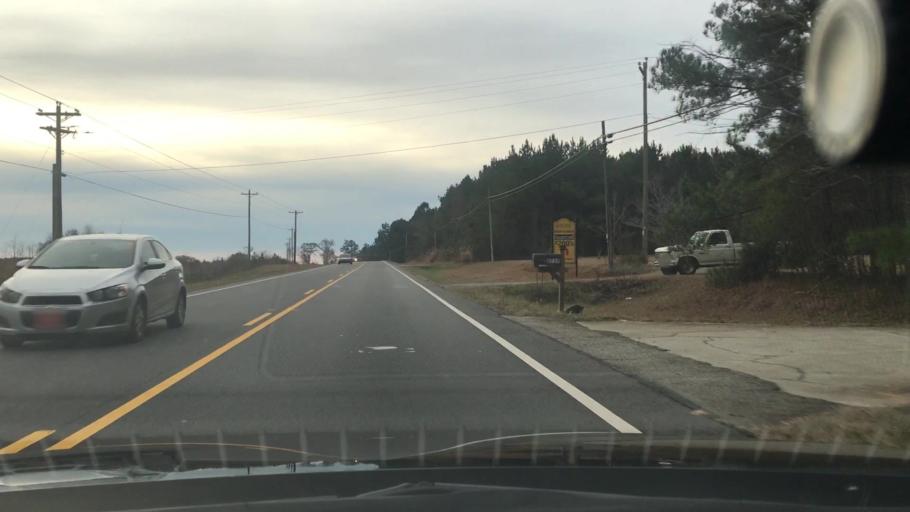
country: US
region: Georgia
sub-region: Coweta County
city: Senoia
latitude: 33.2797
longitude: -84.5352
